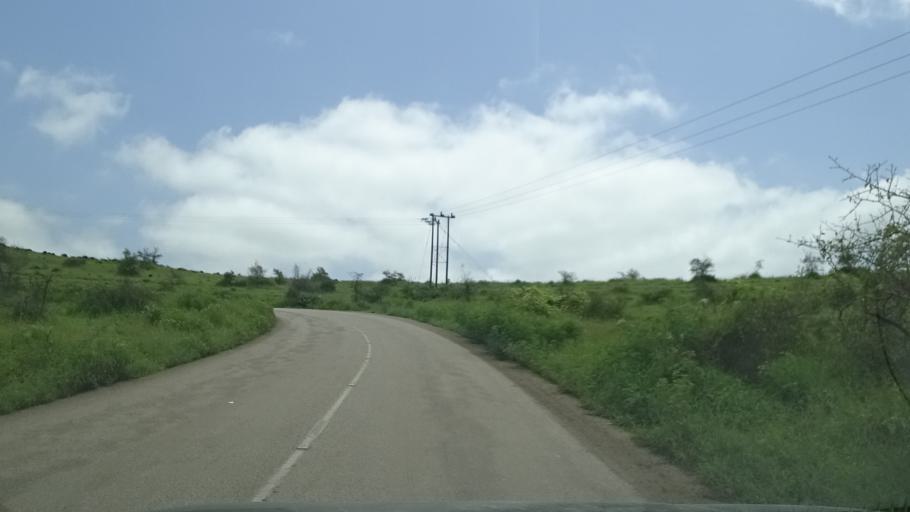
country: OM
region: Zufar
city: Salalah
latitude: 17.2014
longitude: 54.1843
